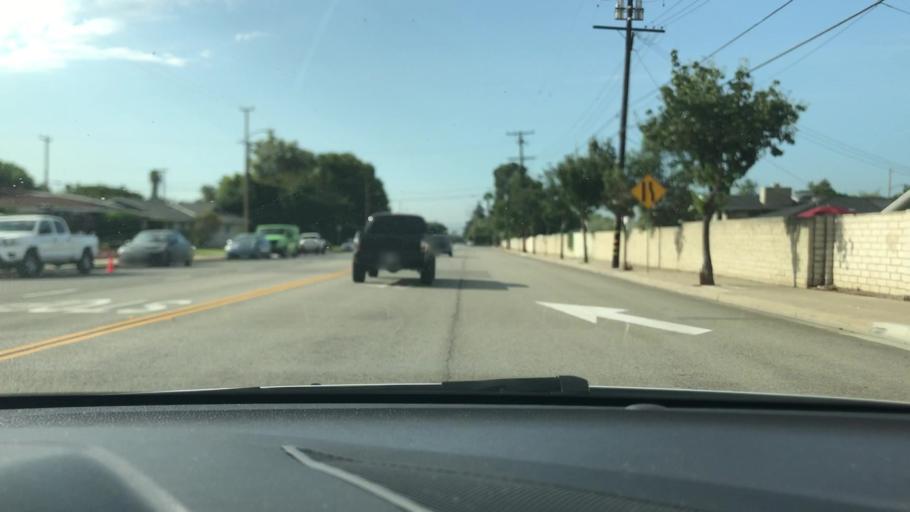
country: US
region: California
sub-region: Orange County
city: North Tustin
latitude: 33.7795
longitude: -117.8184
